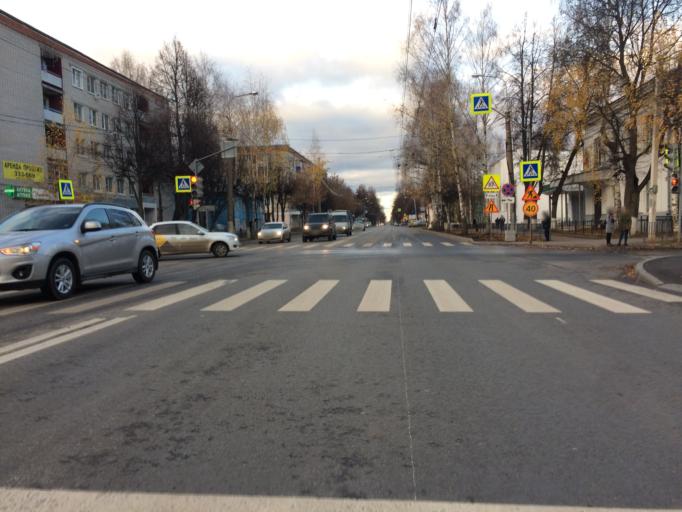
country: RU
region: Mariy-El
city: Yoshkar-Ola
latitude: 56.6437
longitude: 47.8909
